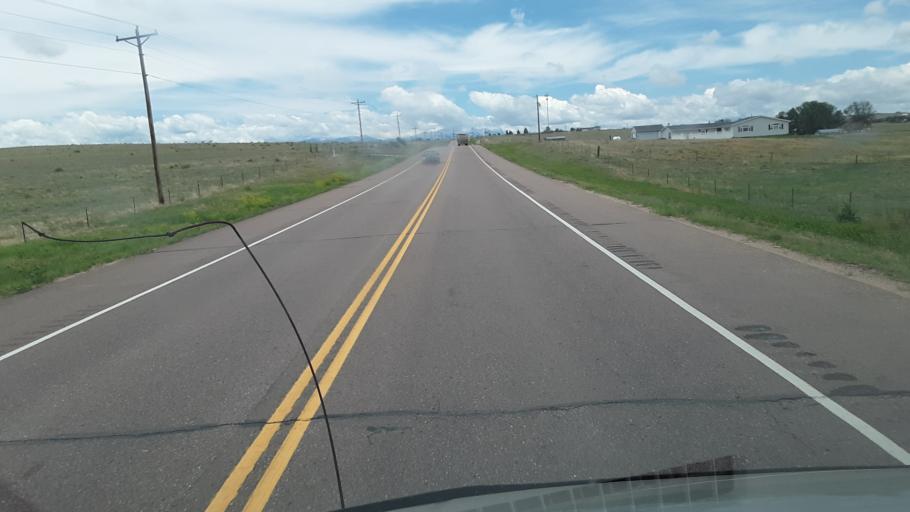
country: US
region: Colorado
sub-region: El Paso County
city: Ellicott
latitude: 38.8386
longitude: -104.5242
